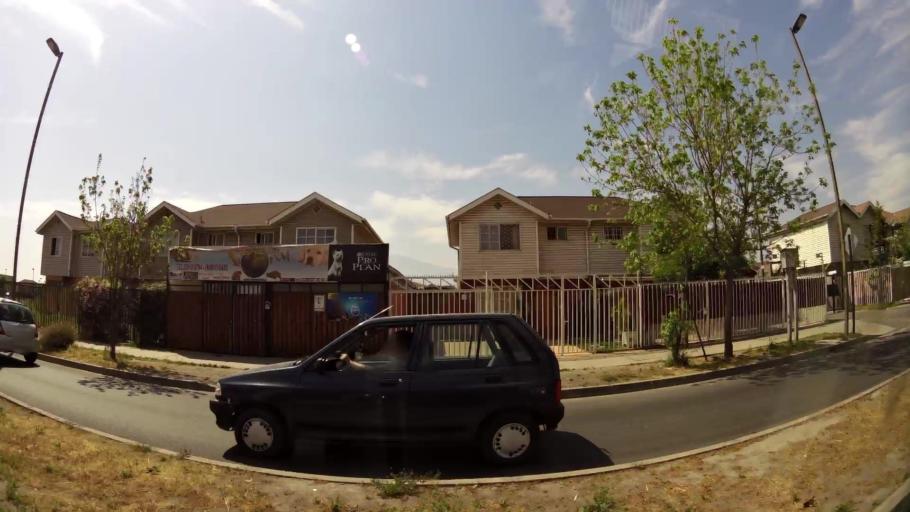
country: CL
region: Santiago Metropolitan
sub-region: Provincia de Cordillera
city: Puente Alto
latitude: -33.5969
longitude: -70.5893
